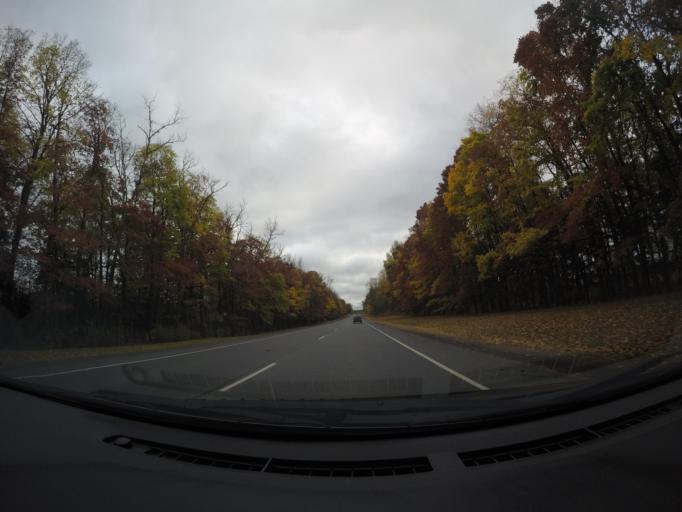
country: RU
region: Moskovskaya
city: Dorokhovo
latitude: 55.5883
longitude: 36.3676
